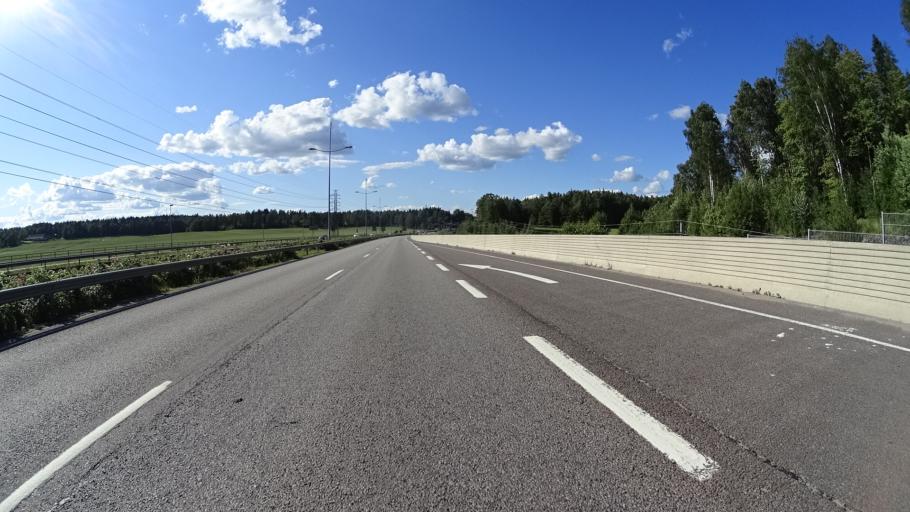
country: FI
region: Uusimaa
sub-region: Helsinki
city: Vantaa
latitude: 60.2485
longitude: 25.1399
